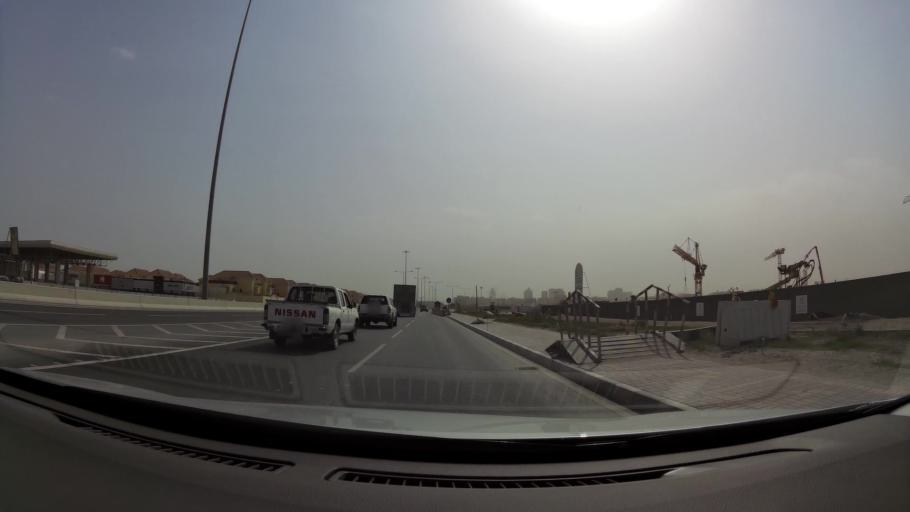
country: QA
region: Baladiyat ad Dawhah
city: Doha
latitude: 25.2941
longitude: 51.4840
